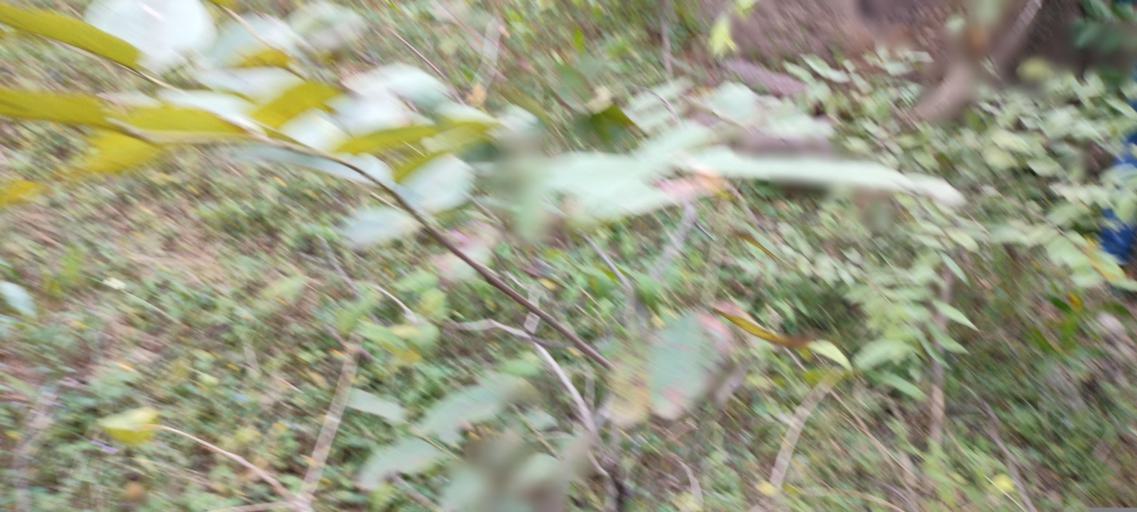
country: IN
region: Telangana
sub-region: Mahbubnagar
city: Farrukhnagar
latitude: 16.8924
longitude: 78.4960
